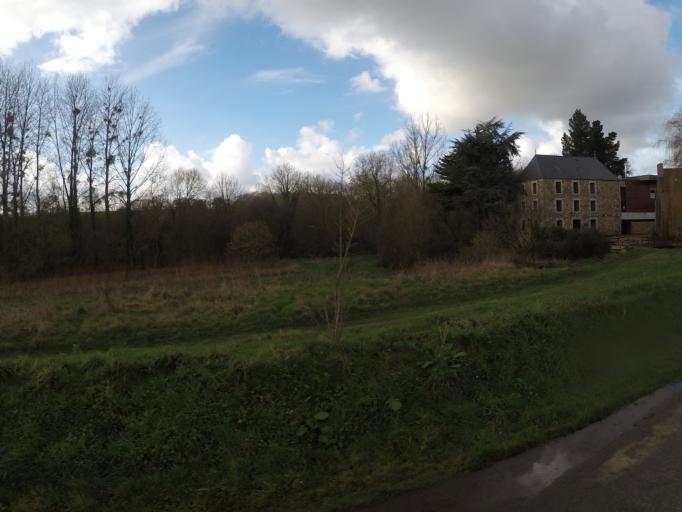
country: FR
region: Brittany
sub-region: Departement des Cotes-d'Armor
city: Lanvollon
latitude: 48.6208
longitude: -2.9976
